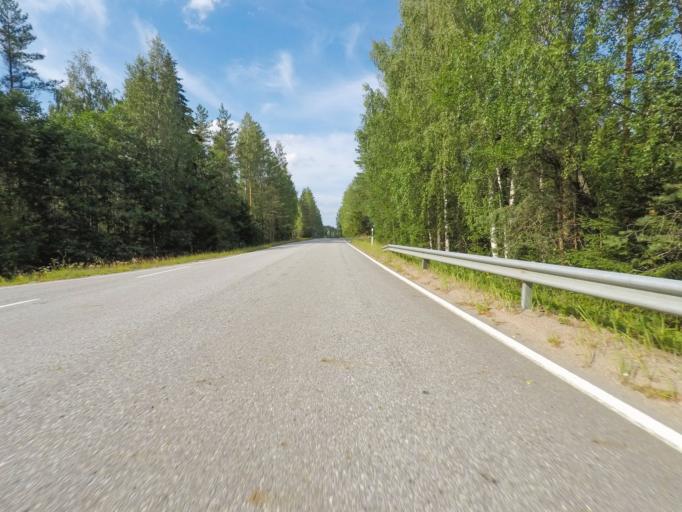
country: FI
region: Southern Savonia
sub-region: Savonlinna
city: Sulkava
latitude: 61.7222
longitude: 28.2057
